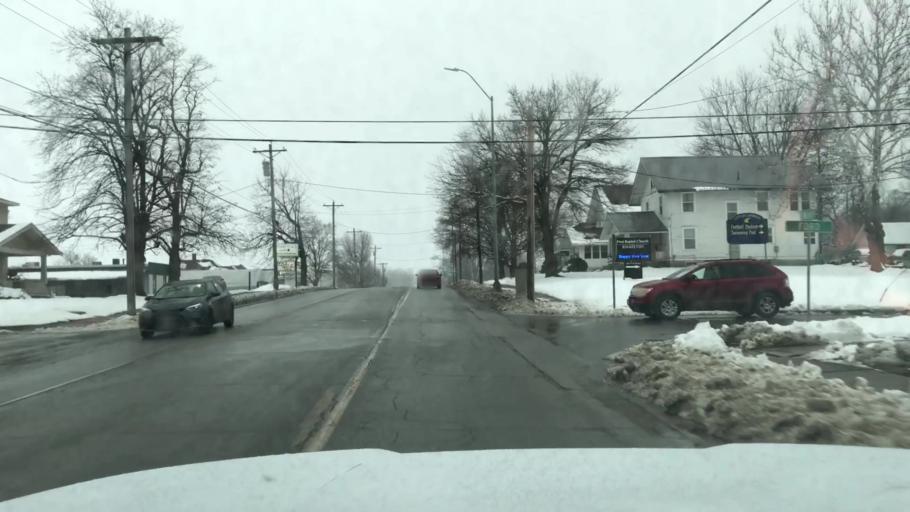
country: US
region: Missouri
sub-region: Clinton County
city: Cameron
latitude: 39.7343
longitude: -94.2361
